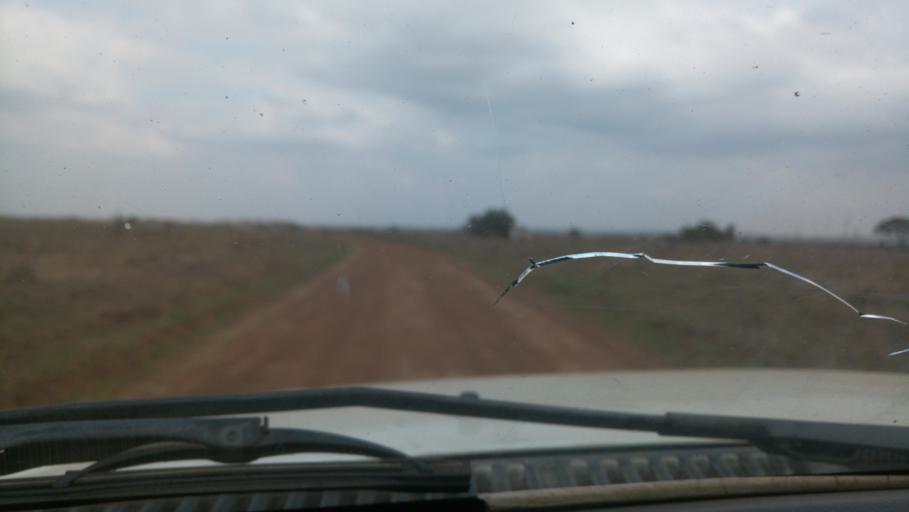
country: KE
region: Nairobi Area
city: Nairobi
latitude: -1.3642
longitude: 36.8304
